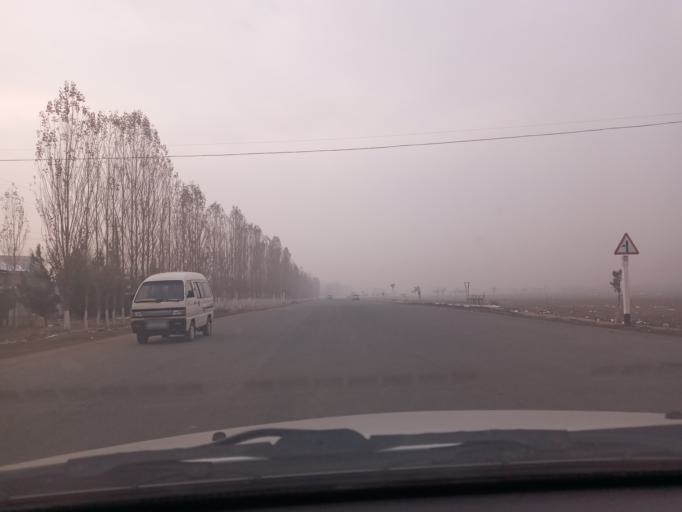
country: UZ
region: Namangan
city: Pop
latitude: 40.9053
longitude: 71.1457
